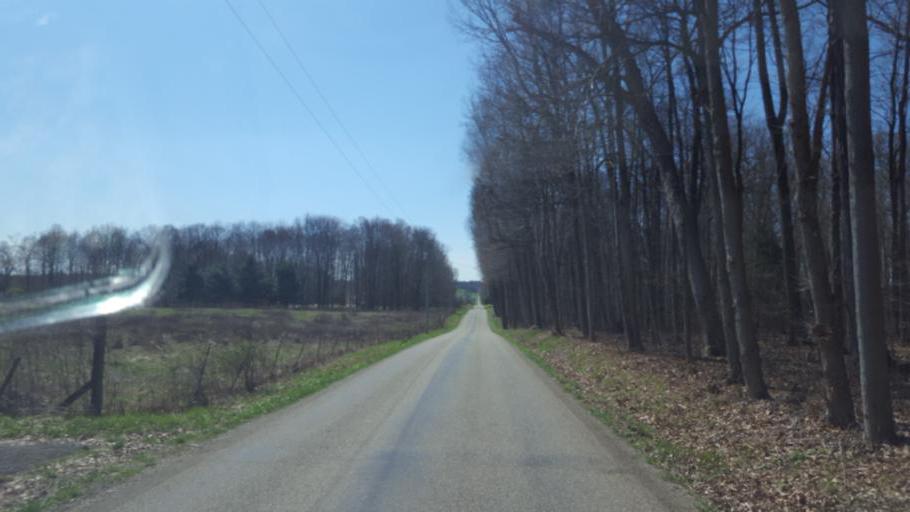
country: US
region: Ohio
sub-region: Knox County
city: Gambier
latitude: 40.3576
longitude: -82.3481
